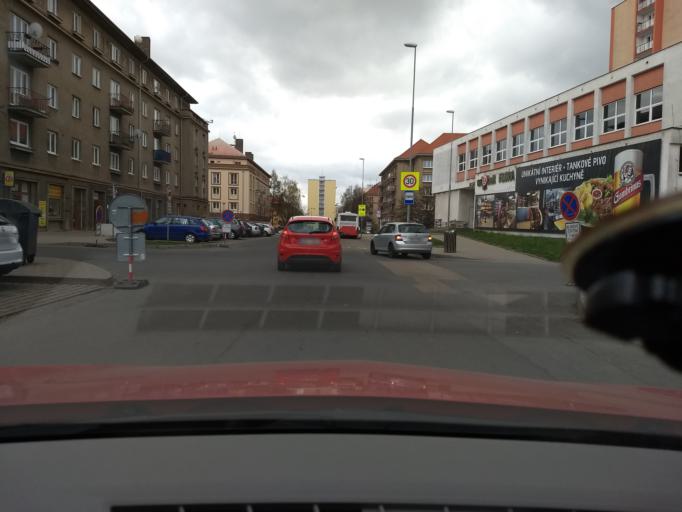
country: CZ
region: Central Bohemia
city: Kladno
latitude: 50.1339
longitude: 14.1212
